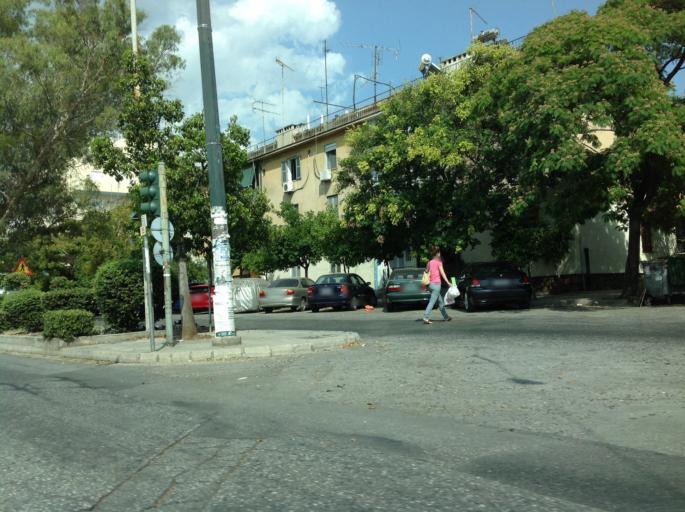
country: GR
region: Attica
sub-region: Nomarchia Athinas
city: Vyronas
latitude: 37.9700
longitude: 23.7544
